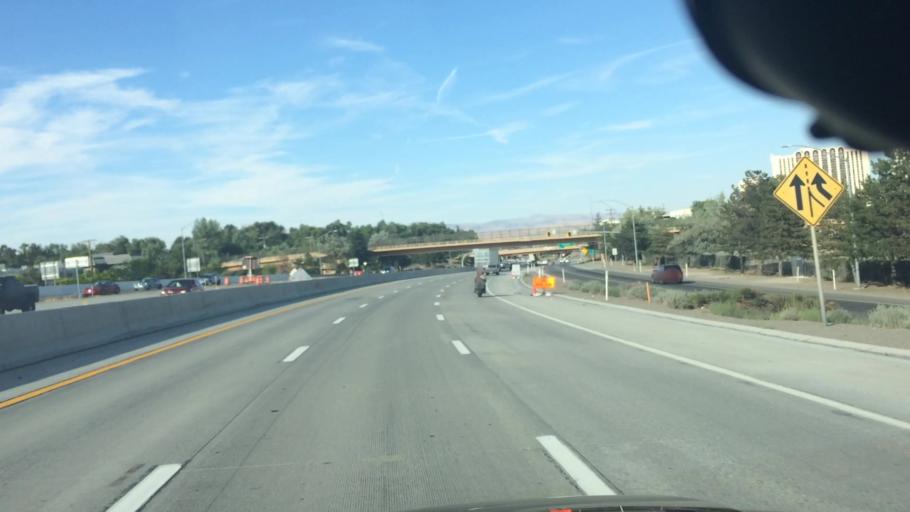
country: US
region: Nevada
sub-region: Washoe County
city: Reno
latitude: 39.5303
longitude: -119.8288
